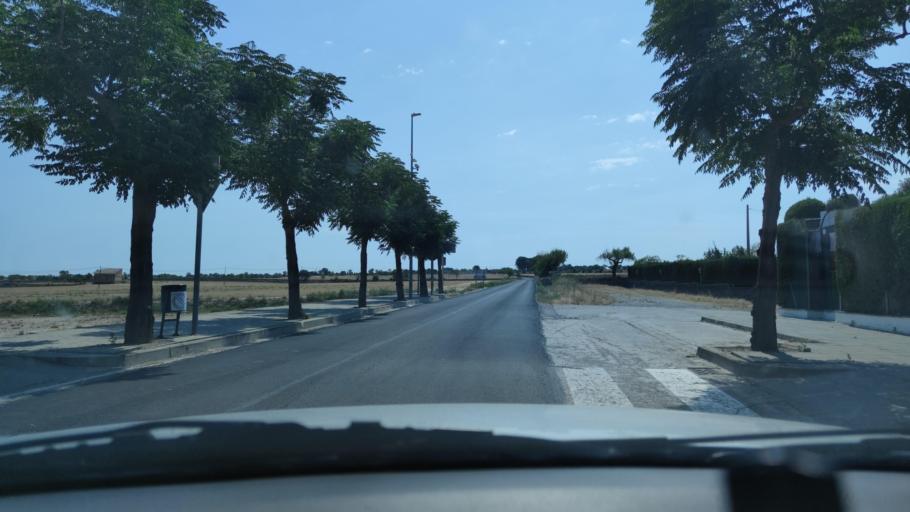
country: ES
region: Catalonia
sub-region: Provincia de Lleida
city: Ivorra
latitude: 41.7835
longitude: 1.2965
